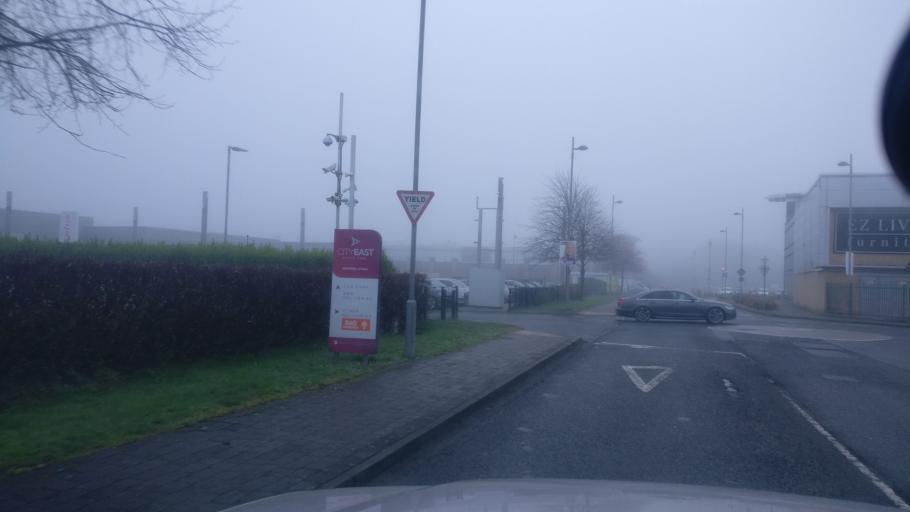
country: IE
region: Munster
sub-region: County Limerick
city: Annacotty
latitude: 52.6495
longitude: -8.5767
